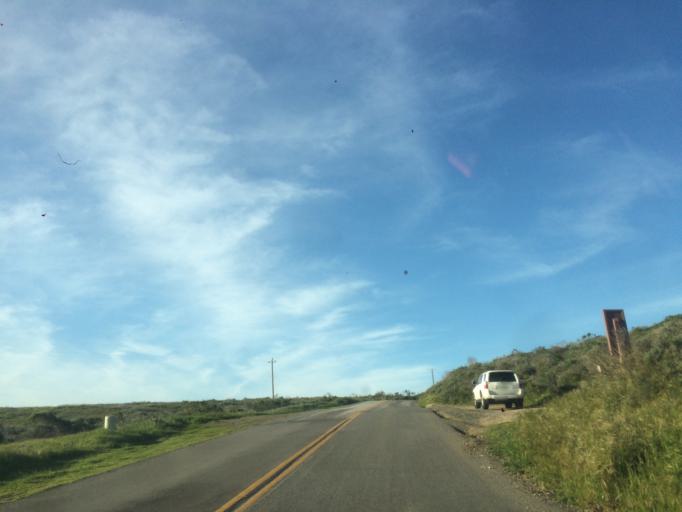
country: US
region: California
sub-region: San Luis Obispo County
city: Los Osos
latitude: 35.2760
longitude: -120.8855
